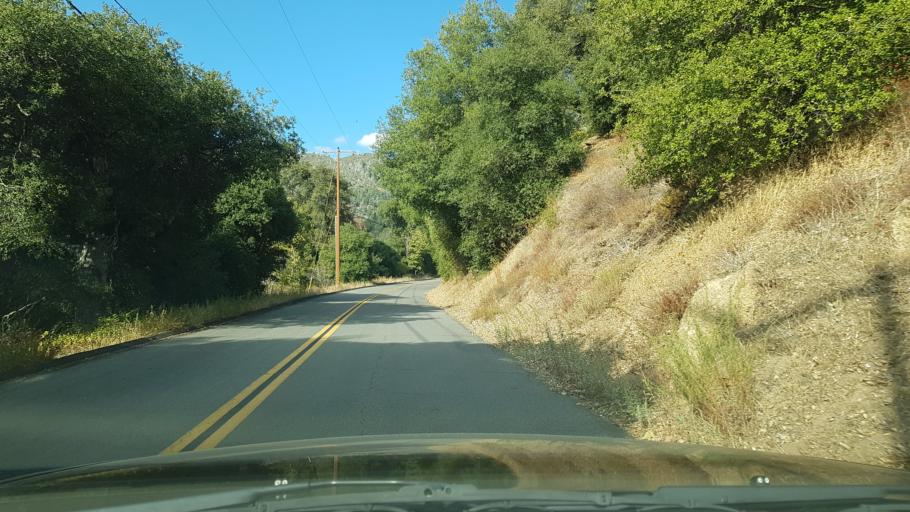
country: US
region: California
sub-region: San Diego County
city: Julian
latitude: 33.1215
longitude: -116.6022
